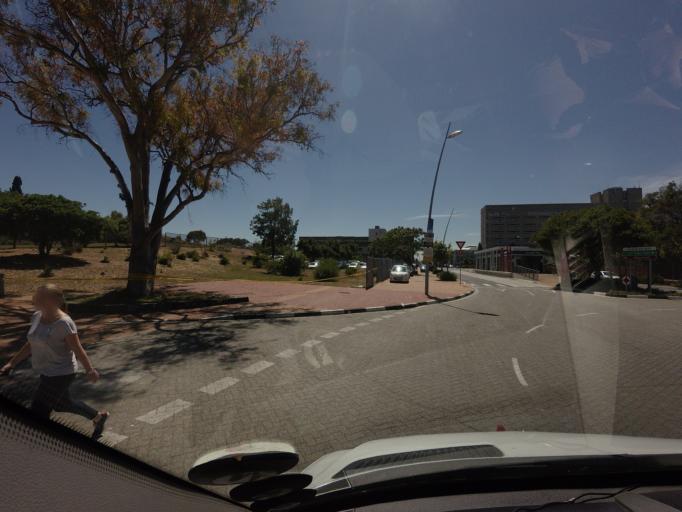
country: ZA
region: Western Cape
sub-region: City of Cape Town
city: Cape Town
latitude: -33.9050
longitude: 18.4139
